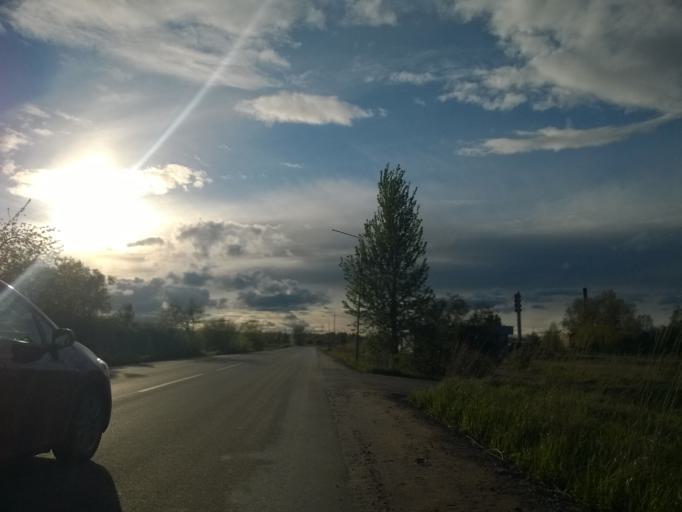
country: LV
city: Tireli
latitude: 56.9344
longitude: 23.6061
